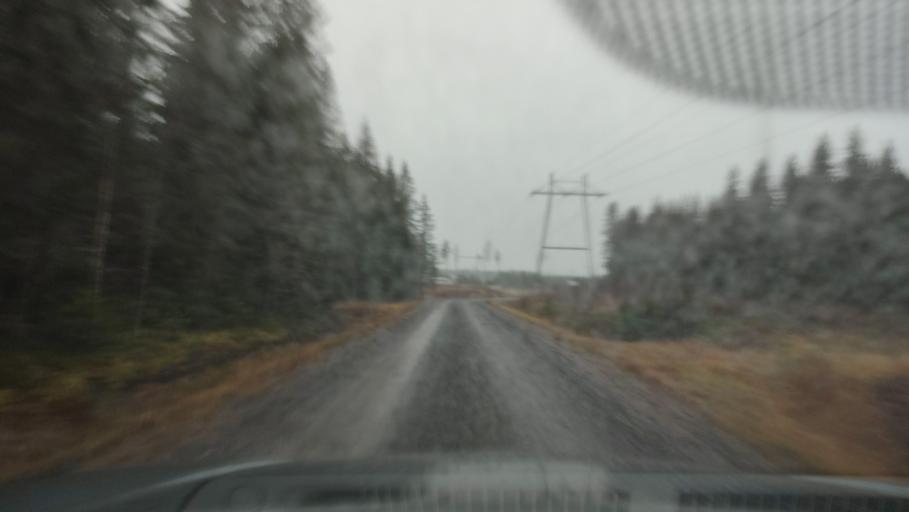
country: FI
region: Southern Ostrobothnia
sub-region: Suupohja
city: Karijoki
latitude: 62.2106
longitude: 21.7297
